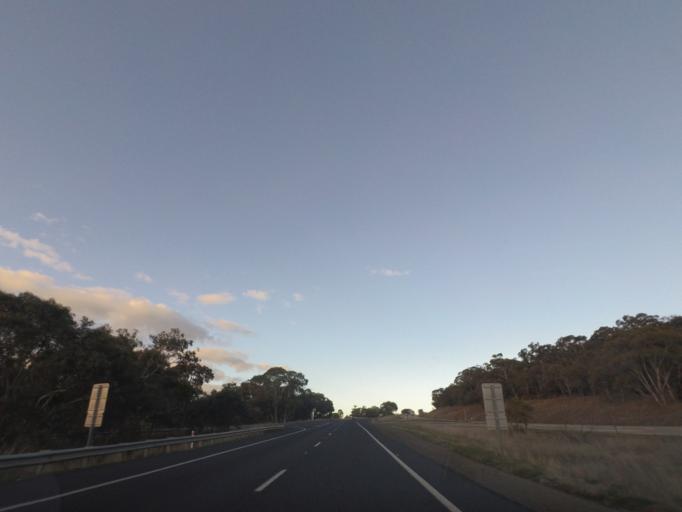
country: AU
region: New South Wales
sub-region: Yass Valley
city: Yass
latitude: -34.7725
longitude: 148.8259
